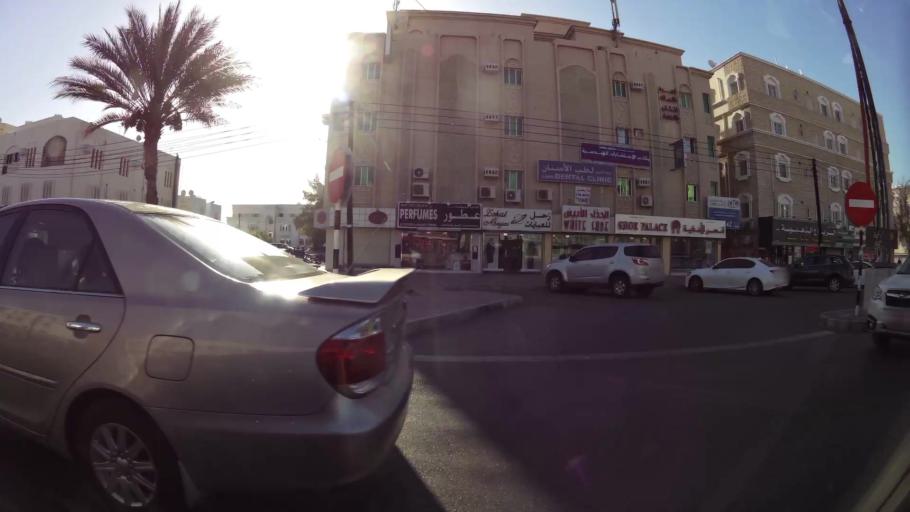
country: OM
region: Muhafazat Masqat
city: As Sib al Jadidah
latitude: 23.6368
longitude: 58.2016
